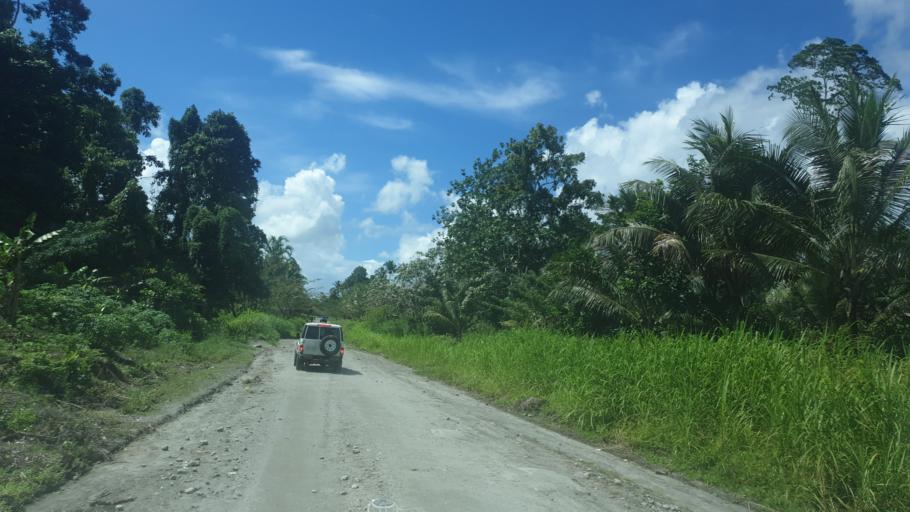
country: PG
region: Bougainville
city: Panguna
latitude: -6.6618
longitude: 155.4551
